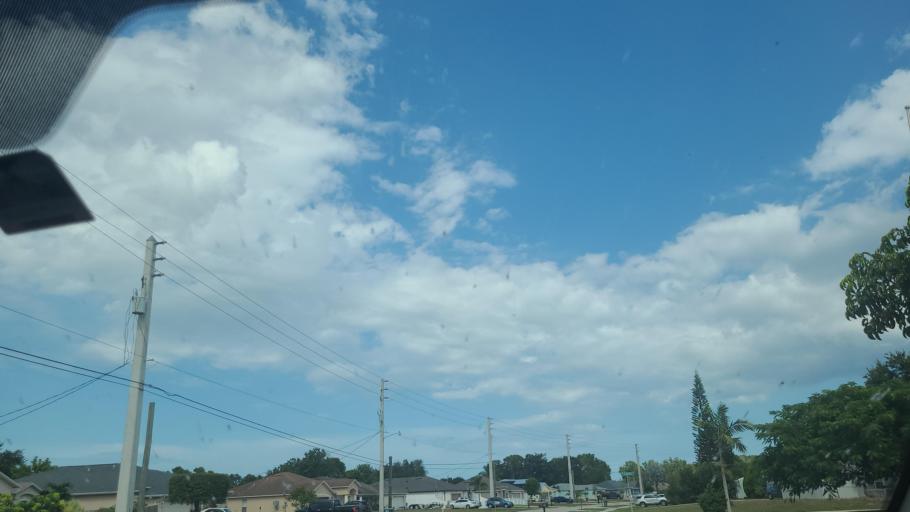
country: US
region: Florida
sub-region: Saint Lucie County
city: Port Saint Lucie
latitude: 27.2563
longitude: -80.3578
